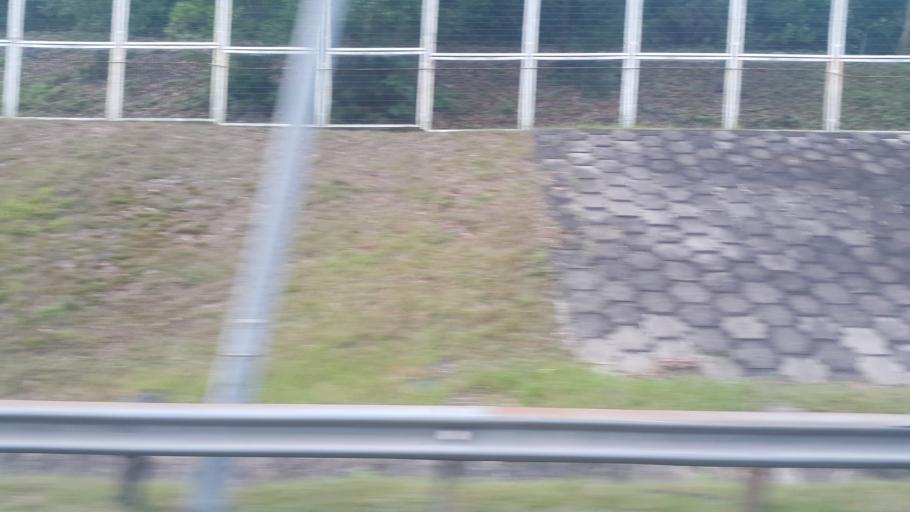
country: MY
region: Johor
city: Pekan Nenas
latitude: 1.3743
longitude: 103.6075
